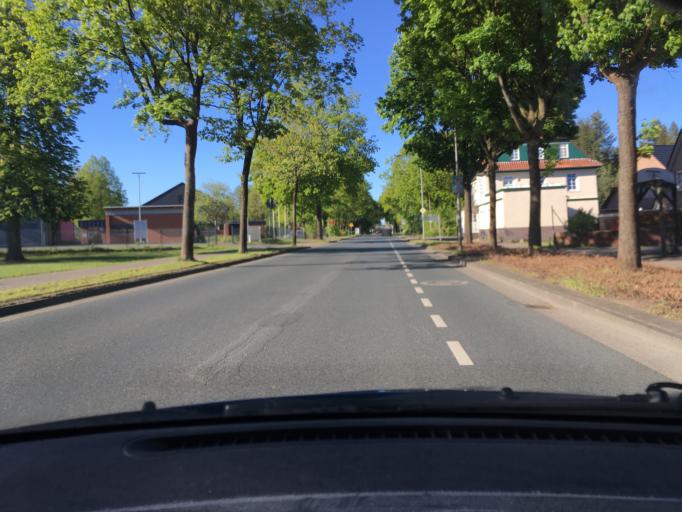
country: DE
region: Lower Saxony
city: Soltau
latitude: 52.9984
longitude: 9.8377
